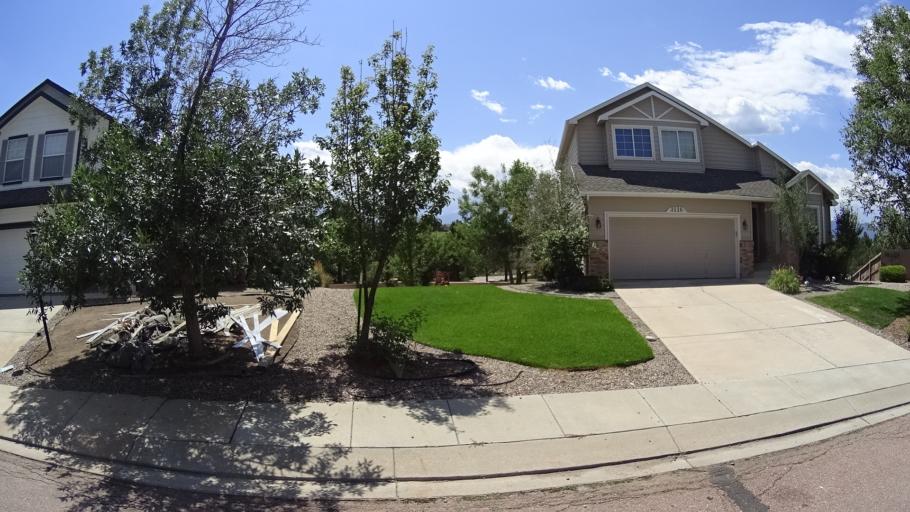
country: US
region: Colorado
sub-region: El Paso County
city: Black Forest
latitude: 38.9674
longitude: -104.7669
